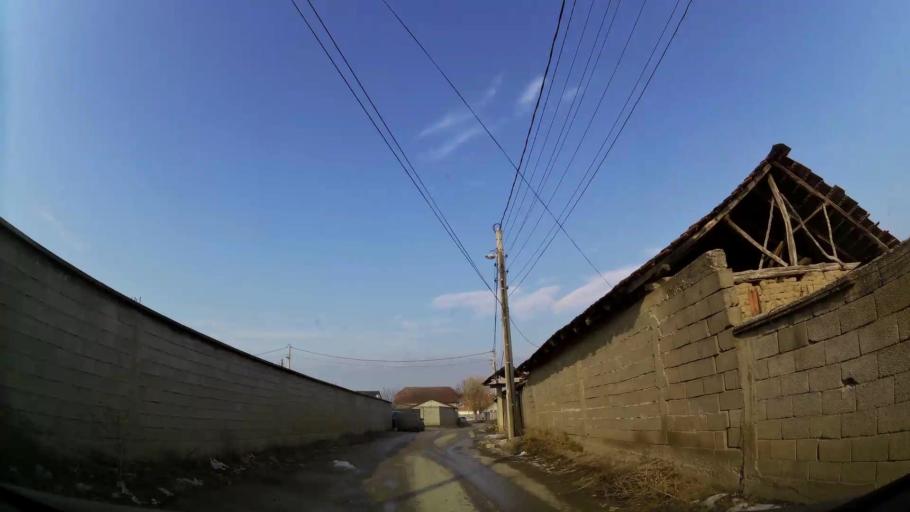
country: MK
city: Creshevo
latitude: 42.0186
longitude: 21.5086
